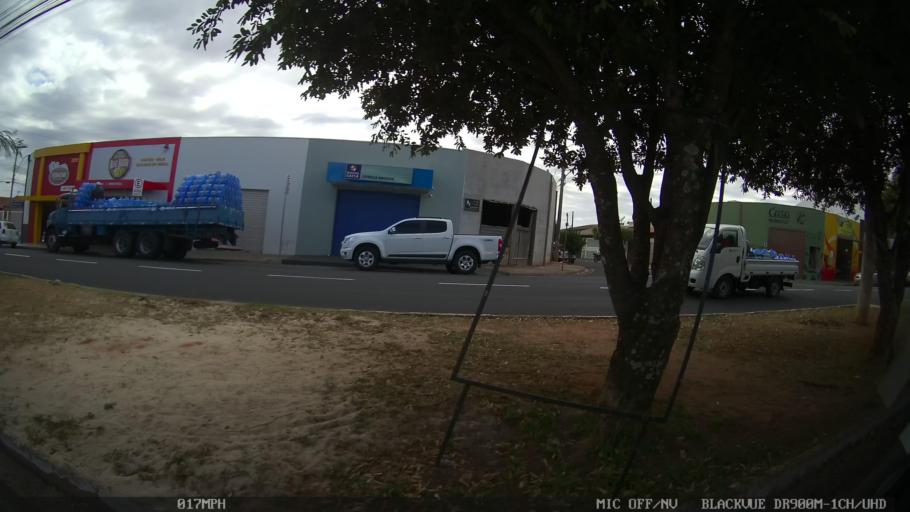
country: BR
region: Sao Paulo
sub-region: Sao Jose Do Rio Preto
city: Sao Jose do Rio Preto
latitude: -20.8040
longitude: -49.4976
